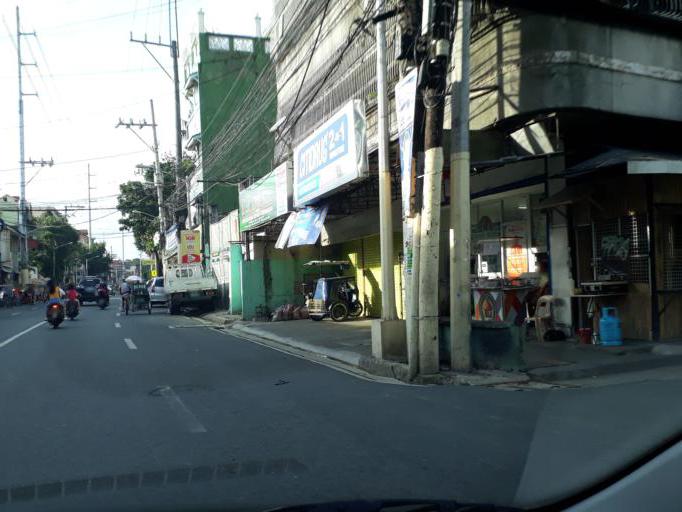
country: PH
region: Metro Manila
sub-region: Caloocan City
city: Niugan
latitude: 14.6474
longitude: 120.9736
